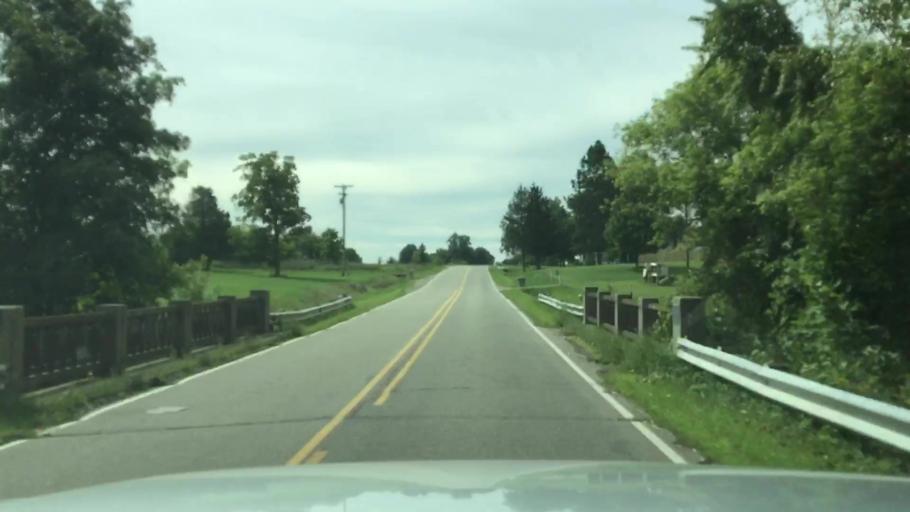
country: US
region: Michigan
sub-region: Genesee County
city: Montrose
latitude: 43.1038
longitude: -83.9878
